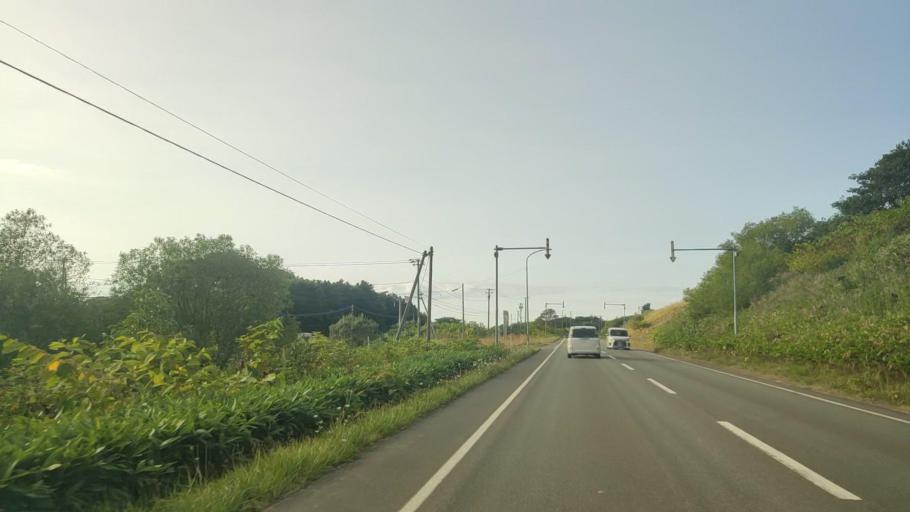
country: JP
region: Hokkaido
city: Makubetsu
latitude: 45.0554
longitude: 141.7492
